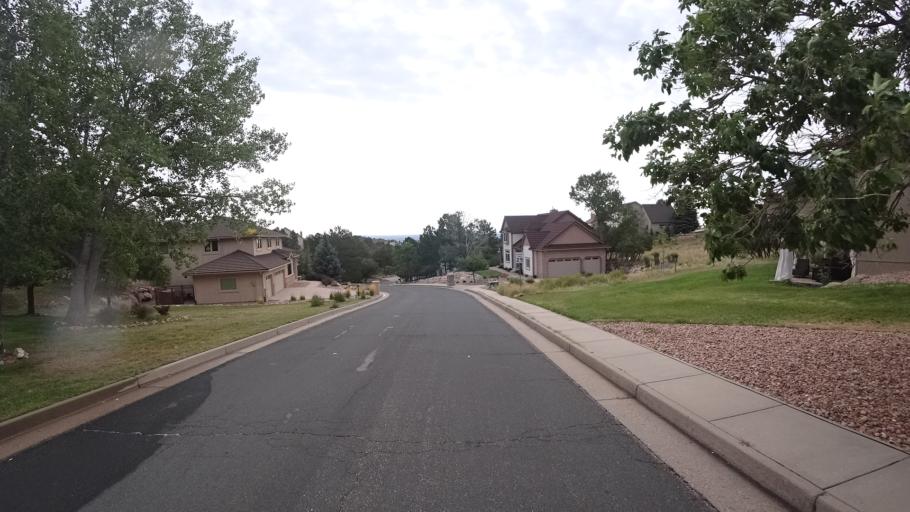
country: US
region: Colorado
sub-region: El Paso County
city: Air Force Academy
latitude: 38.9362
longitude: -104.8656
